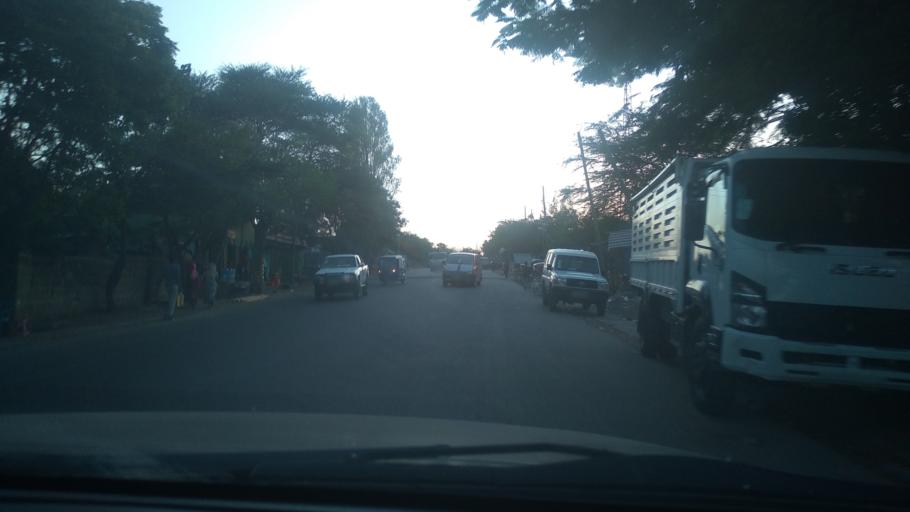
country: ET
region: Oromiya
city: Asbe Teferi
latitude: 9.2332
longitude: 40.7539
